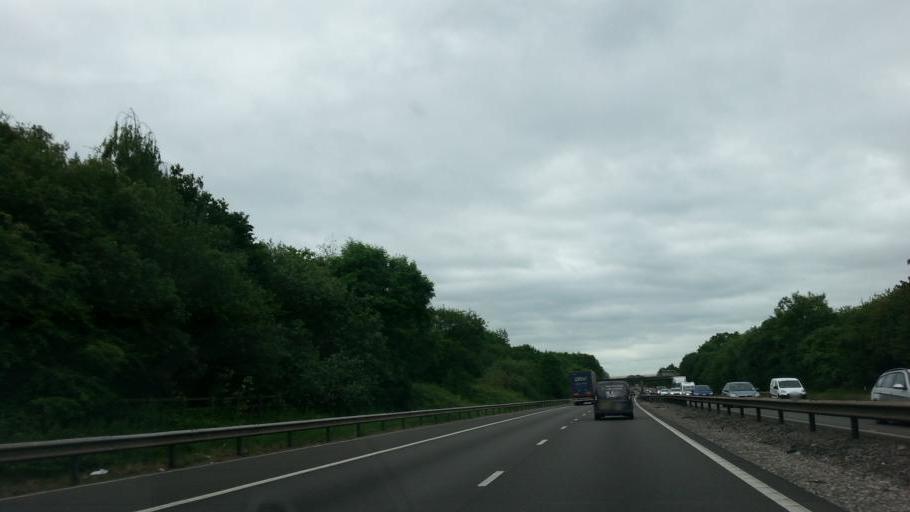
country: GB
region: England
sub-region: Warwickshire
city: Kingsbury
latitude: 52.5646
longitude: -1.6997
